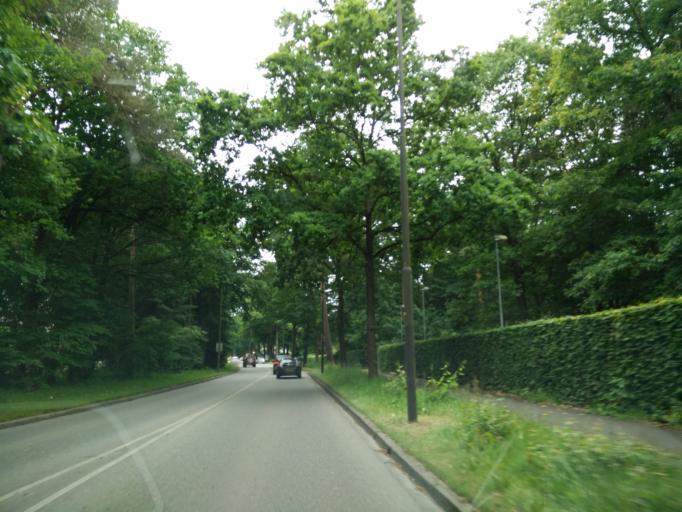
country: NL
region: Gelderland
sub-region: Gemeente Apeldoorn
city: Apeldoorn
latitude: 52.2094
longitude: 5.9306
